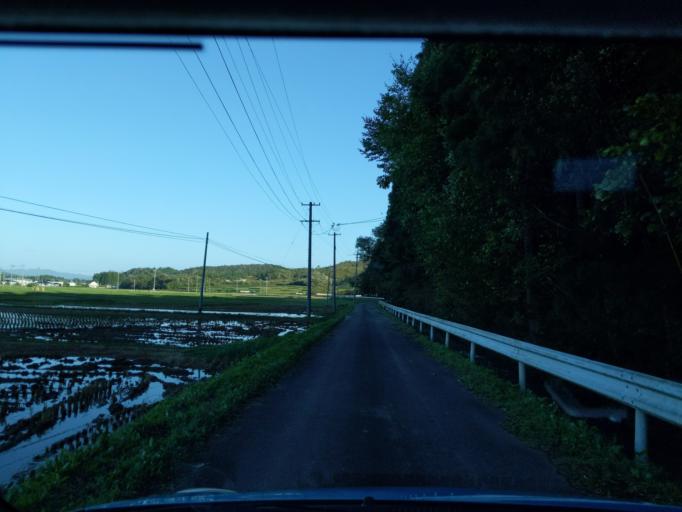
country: JP
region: Iwate
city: Ichinoseki
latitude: 38.9385
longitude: 141.0515
